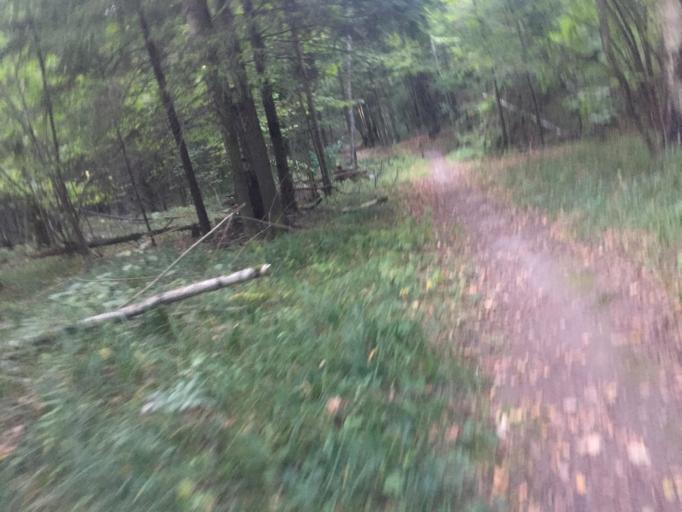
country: RU
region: Moscow
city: Gol'yanovo
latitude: 55.8441
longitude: 37.7880
